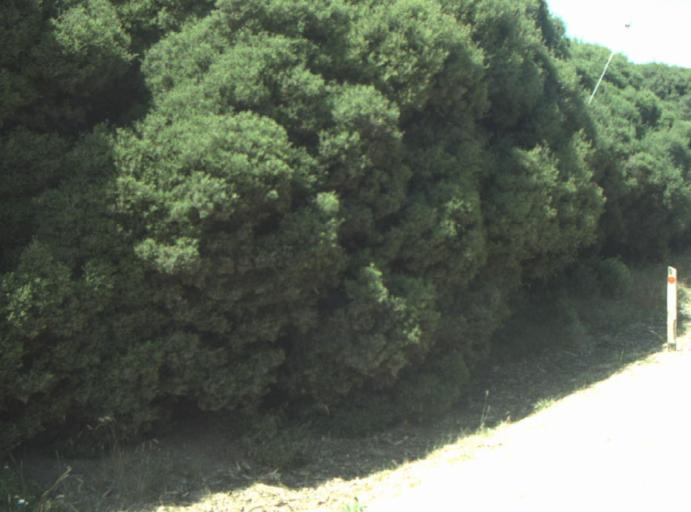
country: AU
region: Victoria
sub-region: Greater Geelong
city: Breakwater
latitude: -38.2745
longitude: 144.4027
